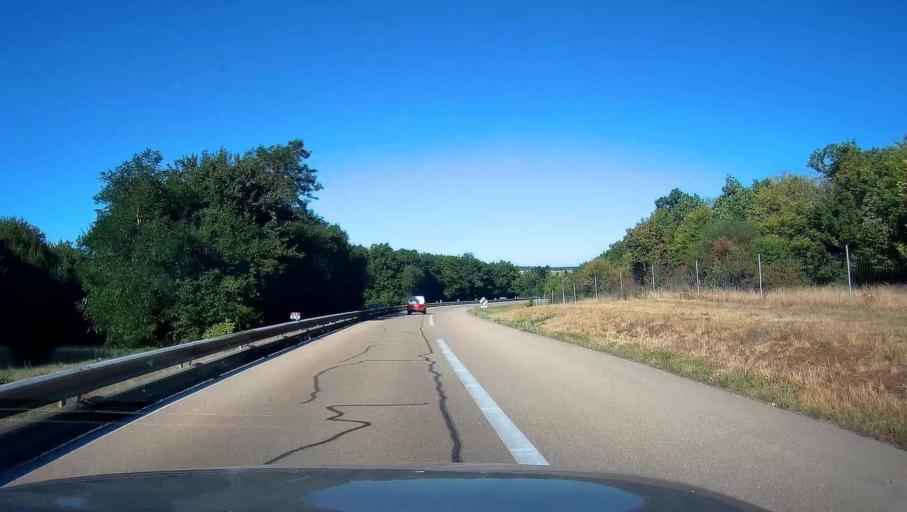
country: FR
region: Champagne-Ardenne
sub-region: Departement de la Haute-Marne
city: Rolampont
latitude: 47.9184
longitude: 5.2252
